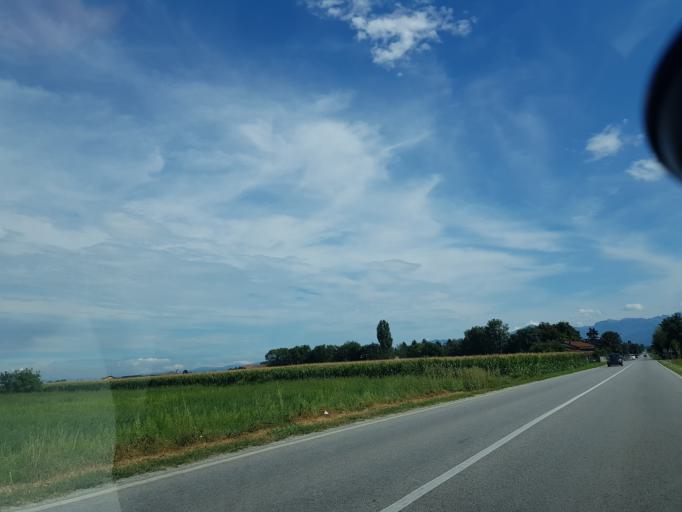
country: IT
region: Piedmont
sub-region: Provincia di Cuneo
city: Roata Rossi
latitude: 44.4660
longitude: 7.5149
